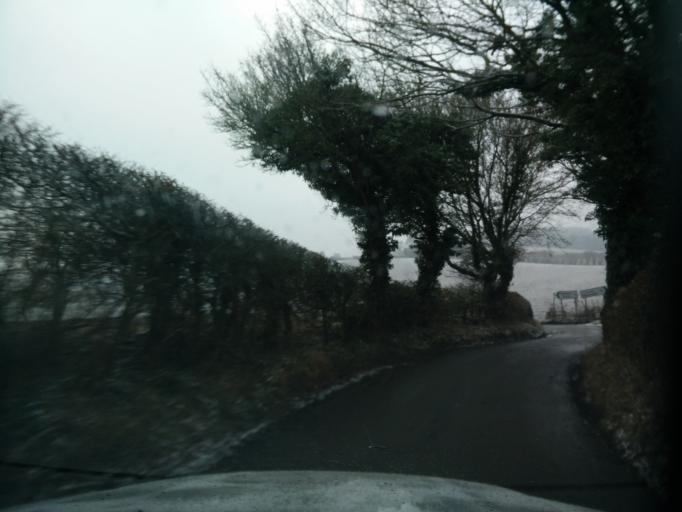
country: GB
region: England
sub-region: Buckinghamshire
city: Great Missenden
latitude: 51.7108
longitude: -0.7415
